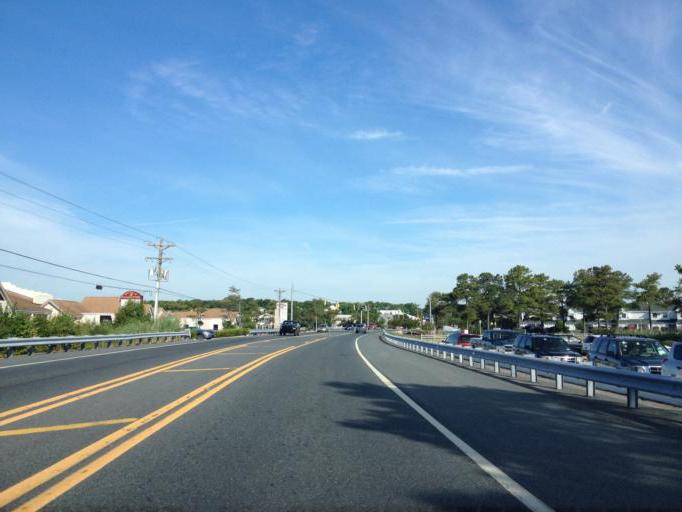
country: US
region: Delaware
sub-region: Sussex County
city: Bethany Beach
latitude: 38.4647
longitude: -75.0837
